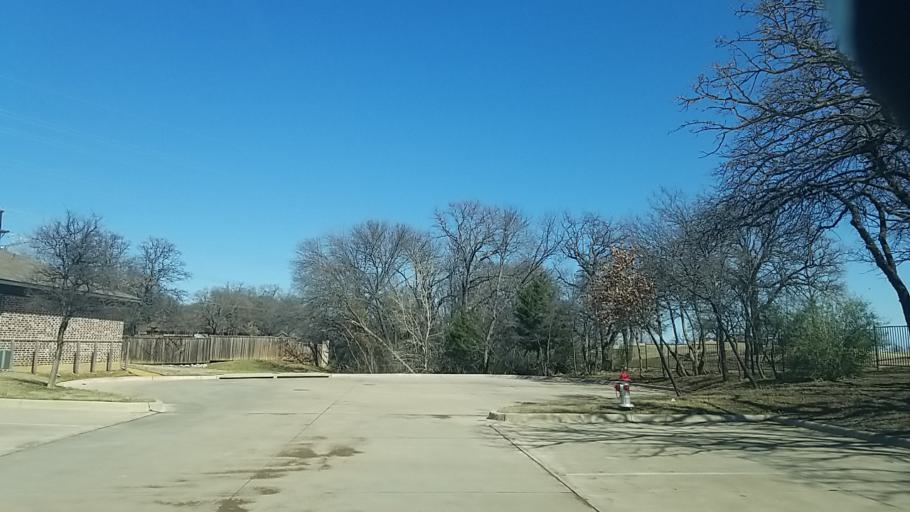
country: US
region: Texas
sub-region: Denton County
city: Corinth
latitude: 33.1589
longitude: -97.0869
